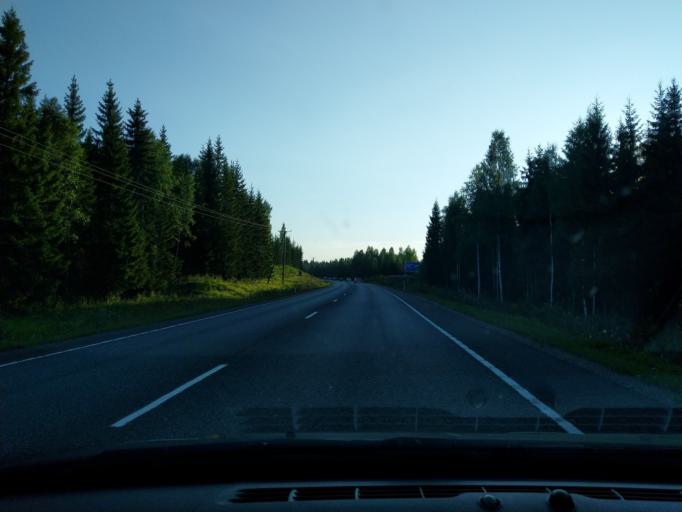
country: FI
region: Uusimaa
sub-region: Helsinki
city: Maentsaelae
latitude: 60.6261
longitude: 25.1656
